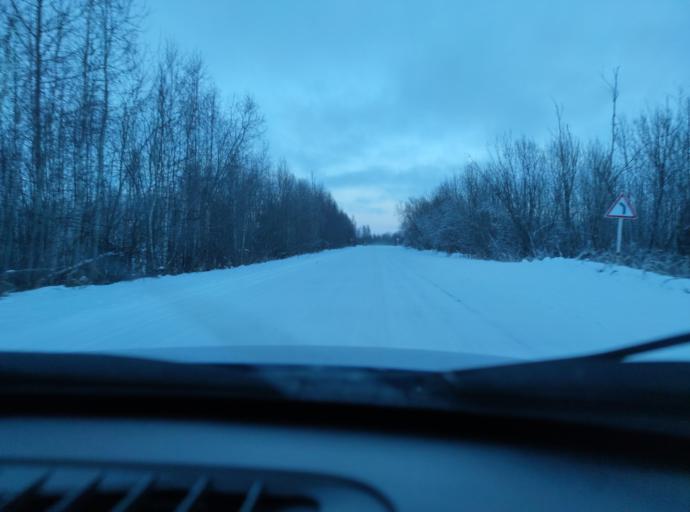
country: RU
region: Khanty-Mansiyskiy Avtonomnyy Okrug
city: Langepas
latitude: 61.1510
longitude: 75.1604
